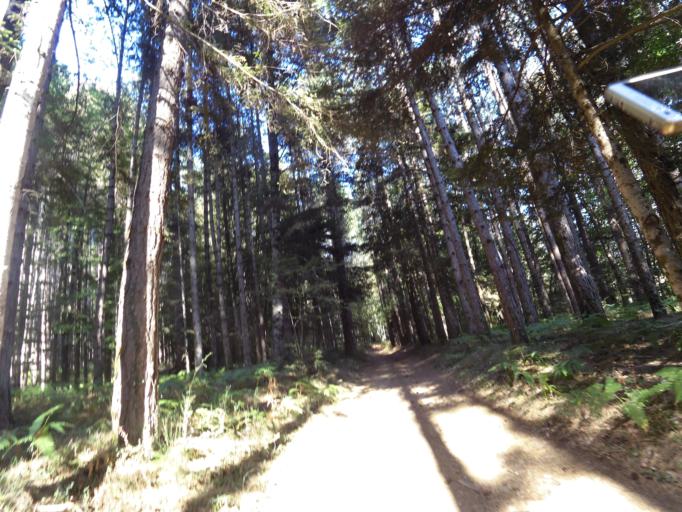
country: IT
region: Calabria
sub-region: Provincia di Vibo-Valentia
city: Nardodipace
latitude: 38.5127
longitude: 16.3724
